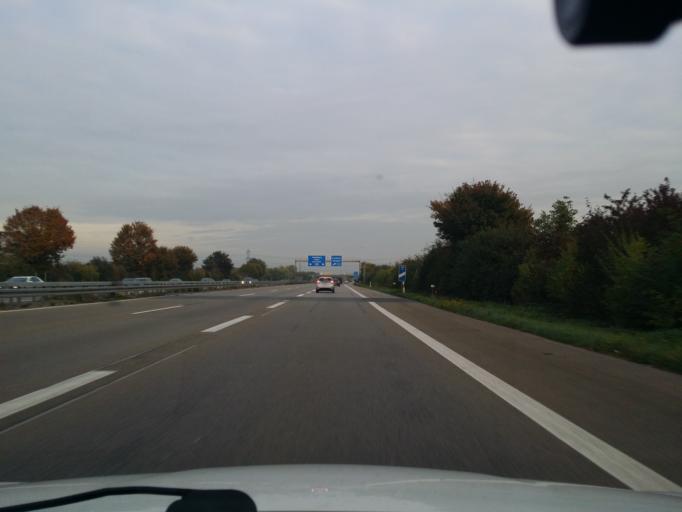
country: DE
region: Baden-Wuerttemberg
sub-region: Karlsruhe Region
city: Ilvesheim
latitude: 49.4641
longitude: 8.5299
